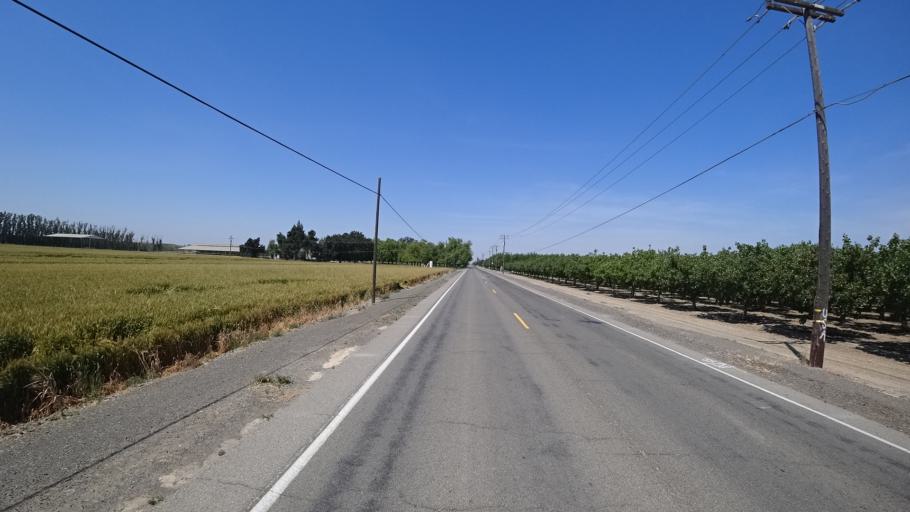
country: US
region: California
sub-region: Fresno County
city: Laton
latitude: 36.4011
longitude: -119.7029
